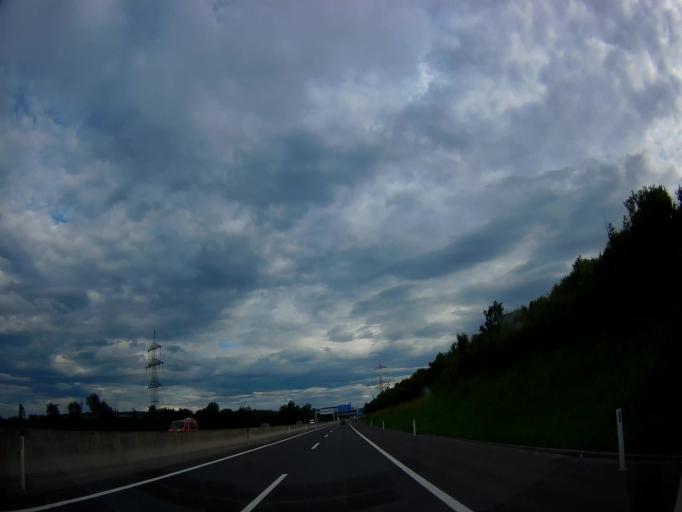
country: AT
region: Lower Austria
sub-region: Politischer Bezirk Sankt Polten
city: Traismauer
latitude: 48.3588
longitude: 15.7210
